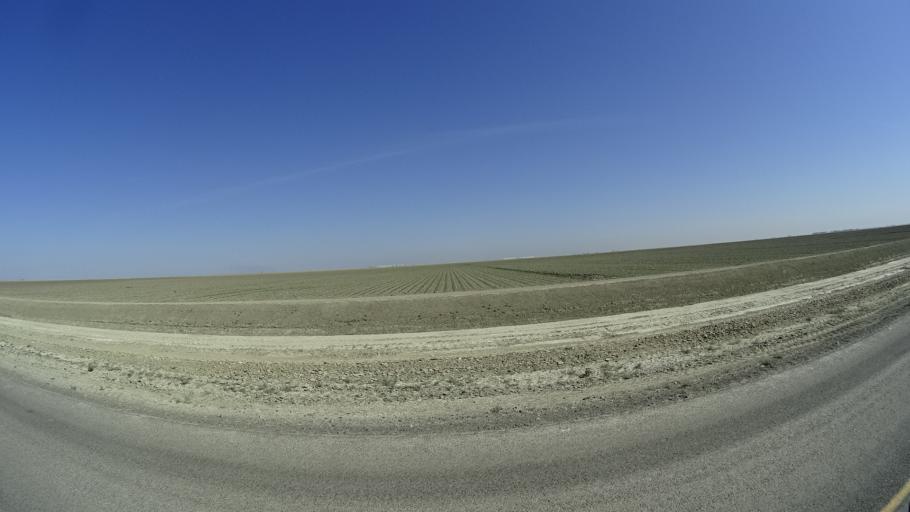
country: US
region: California
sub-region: Tulare County
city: Alpaugh
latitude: 35.8913
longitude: -119.5621
